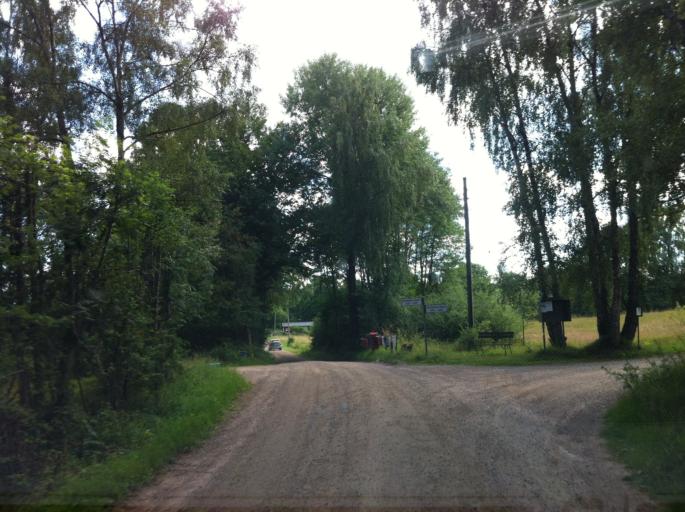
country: SE
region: Skane
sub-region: Astorps Kommun
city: Kvidinge
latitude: 56.1028
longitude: 13.0725
